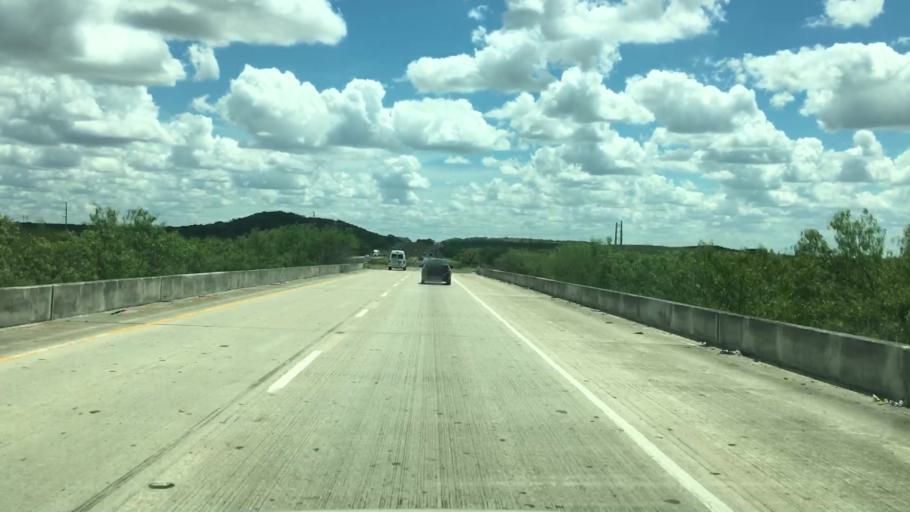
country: US
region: Texas
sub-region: Live Oak County
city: Three Rivers
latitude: 28.7316
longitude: -98.2887
